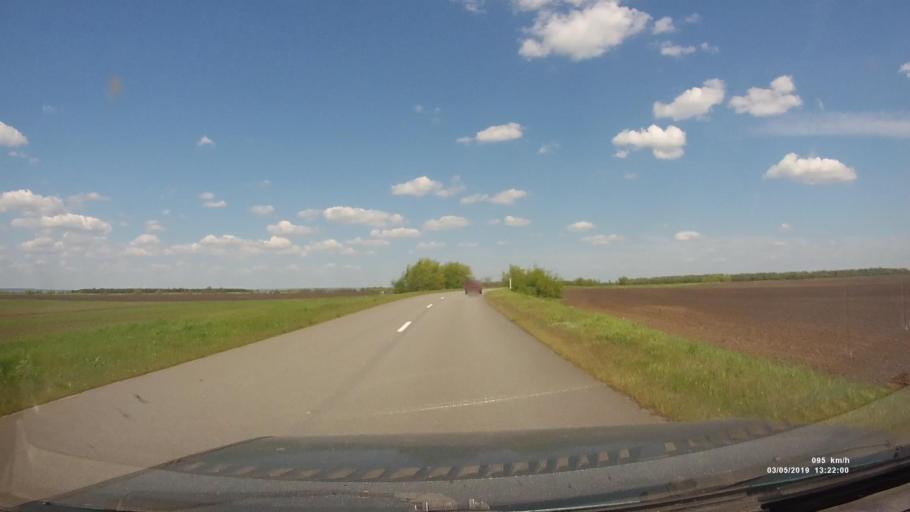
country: RU
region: Rostov
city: Semikarakorsk
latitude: 47.5584
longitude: 40.7509
